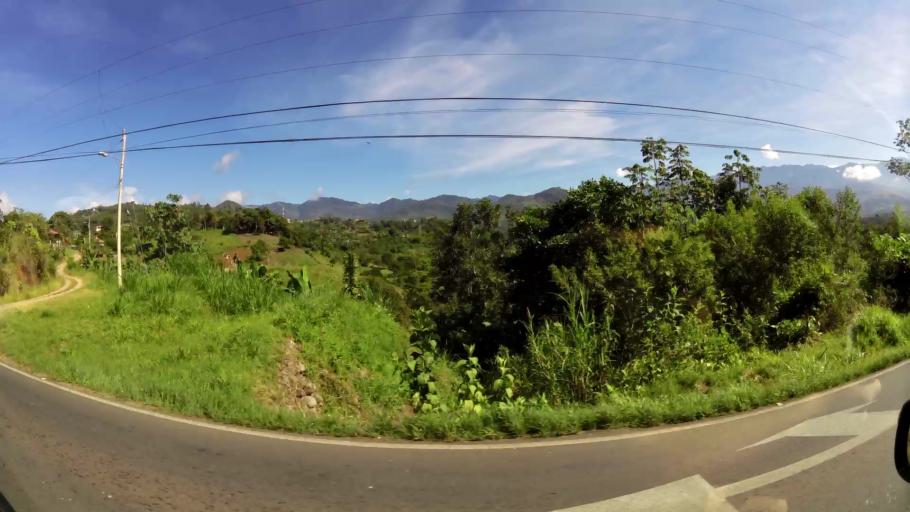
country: CR
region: San Jose
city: San Isidro
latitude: 9.3951
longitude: -83.7136
